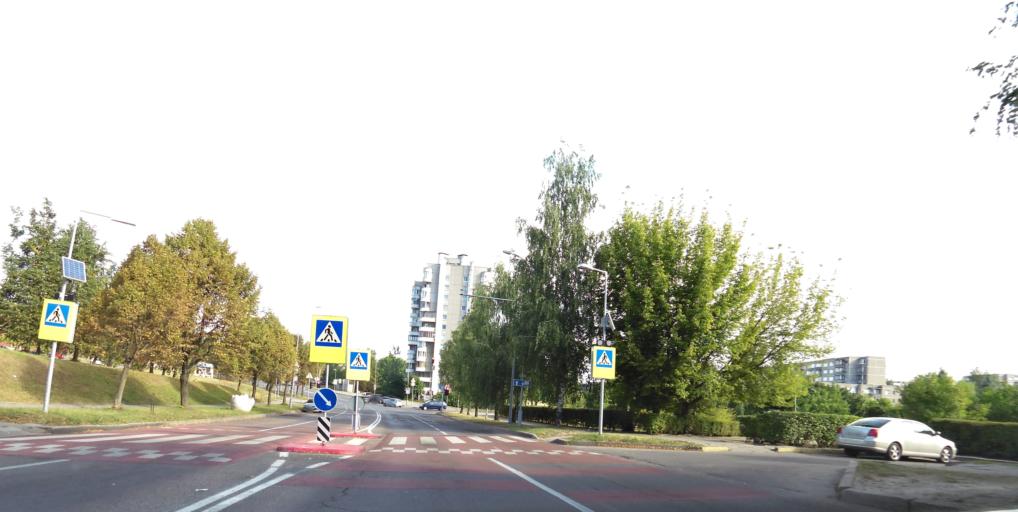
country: LT
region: Vilnius County
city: Seskine
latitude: 54.7149
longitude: 25.2516
